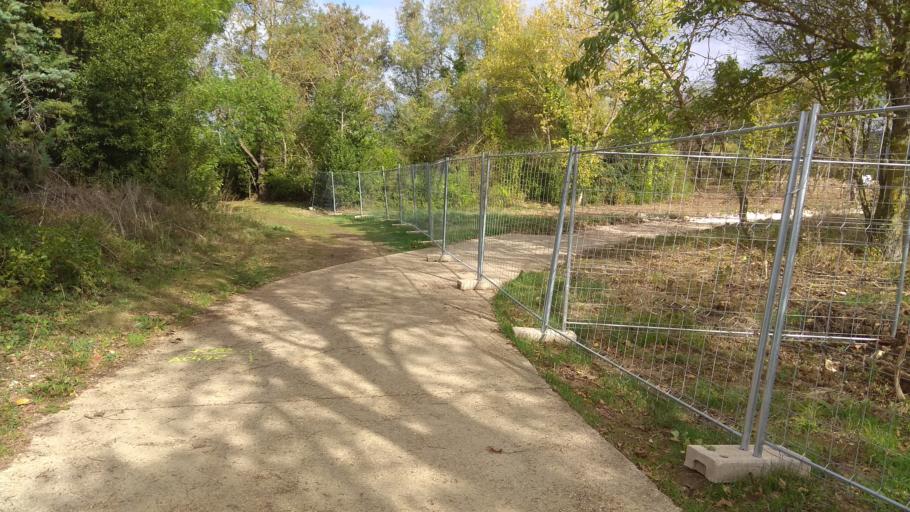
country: ES
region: Navarre
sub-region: Provincia de Navarra
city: Cizur Mayor
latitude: 42.8026
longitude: -1.6968
